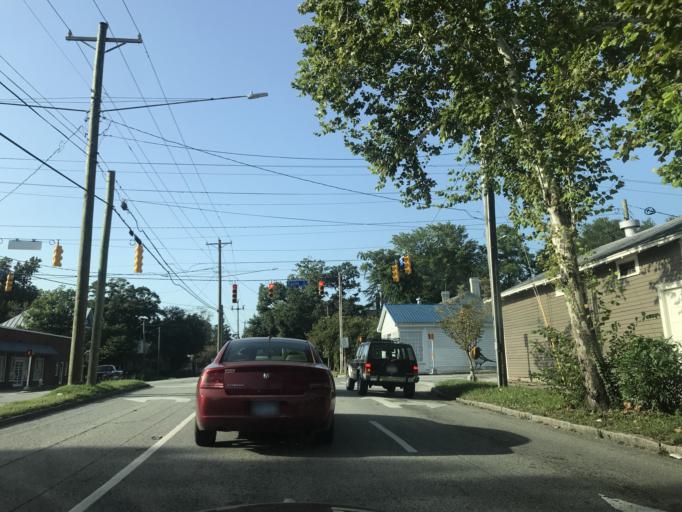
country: US
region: North Carolina
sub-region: New Hanover County
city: Wilmington
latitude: 34.2277
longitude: -77.9451
